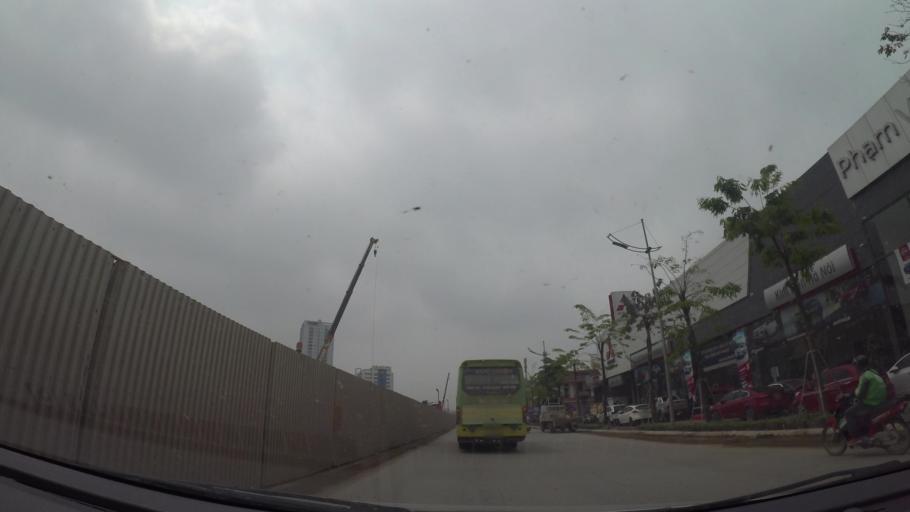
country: VN
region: Ha Noi
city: Tay Ho
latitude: 21.0725
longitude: 105.7853
